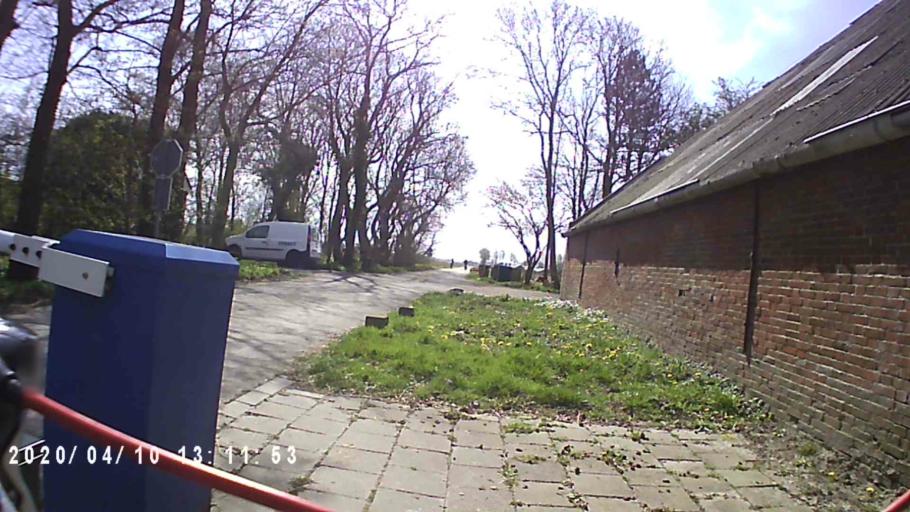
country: NL
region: Groningen
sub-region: Gemeente De Marne
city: Ulrum
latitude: 53.4044
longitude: 6.4181
